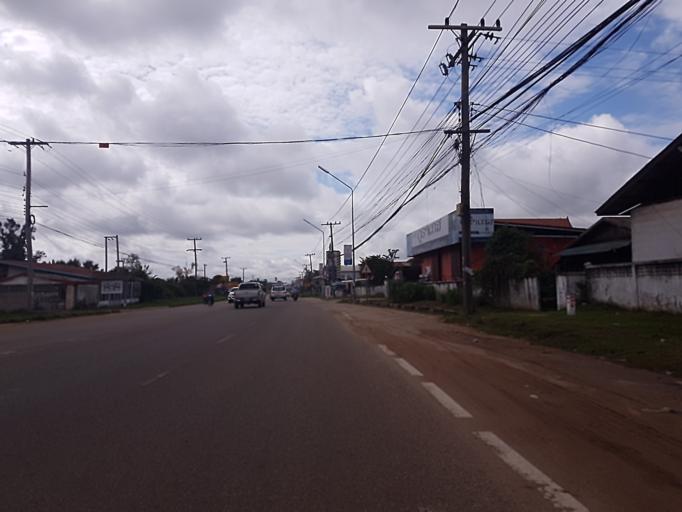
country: TH
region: Nong Khai
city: Tha Bo
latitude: 17.8887
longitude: 102.6466
